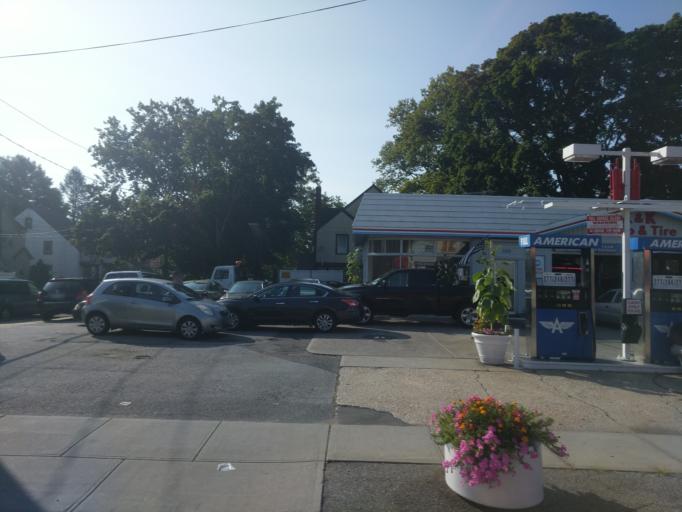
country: US
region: New York
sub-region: Nassau County
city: West Hempstead
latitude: 40.7004
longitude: -73.6489
